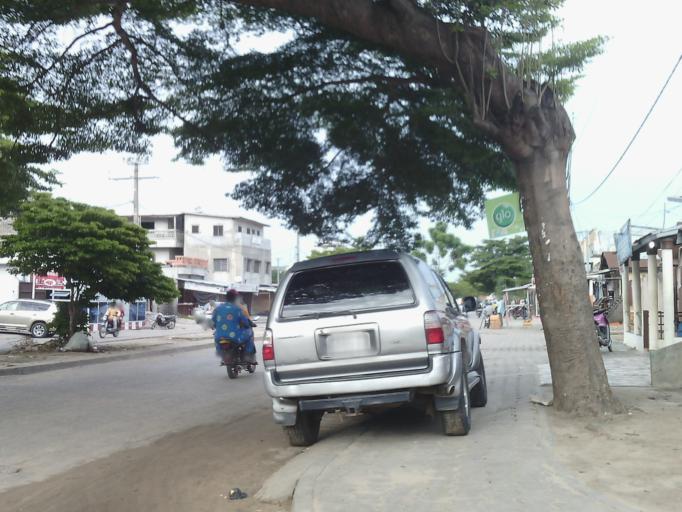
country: BJ
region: Atlantique
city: Abomey-Calavi
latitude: 6.3923
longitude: 2.3619
